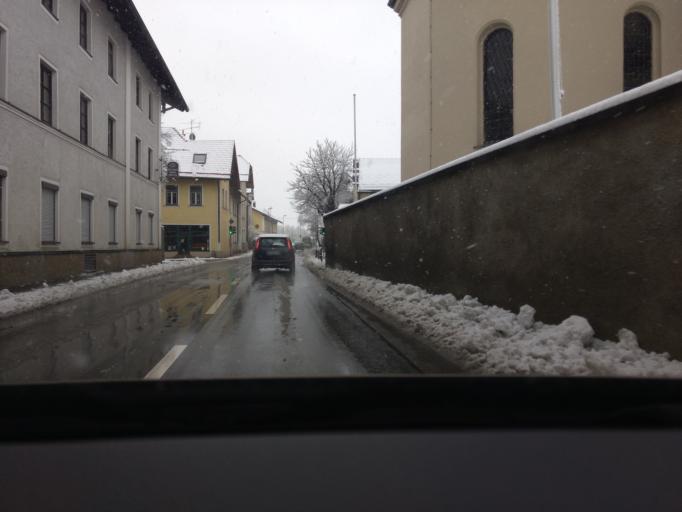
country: DE
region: Bavaria
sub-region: Upper Bavaria
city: Vachendorf
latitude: 47.8608
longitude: 12.6281
